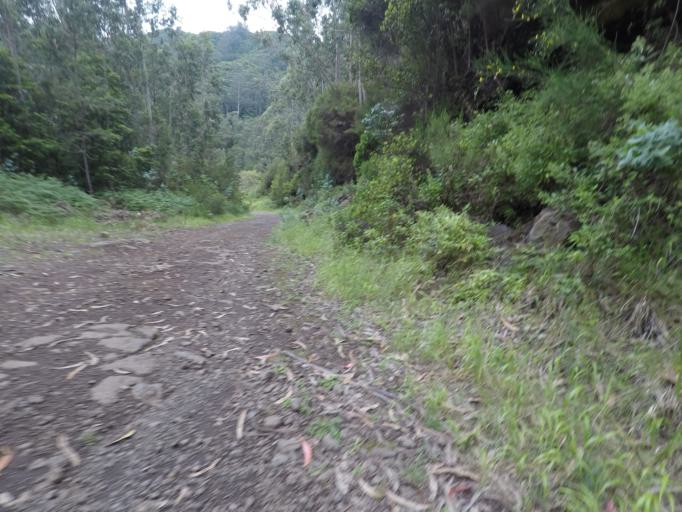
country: PT
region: Madeira
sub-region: Sao Vicente
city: Sao Vicente
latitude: 32.7742
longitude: -17.0483
